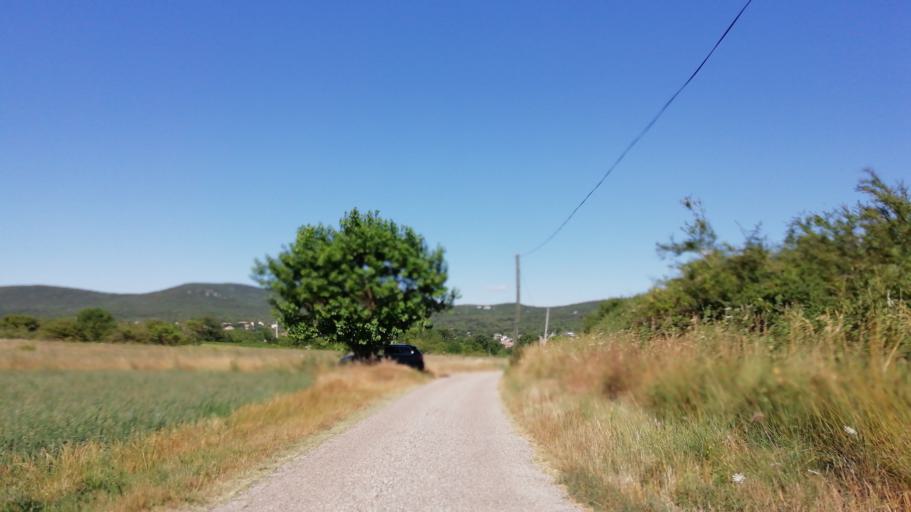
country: FR
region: Languedoc-Roussillon
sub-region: Departement de l'Herault
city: Saint-Martin-de-Londres
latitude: 43.7892
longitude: 3.7426
